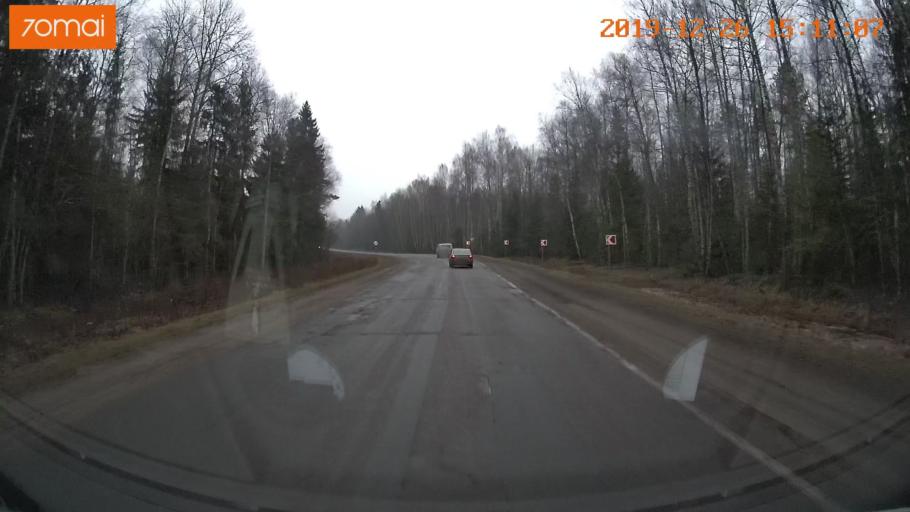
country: RU
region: Jaroslavl
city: Rybinsk
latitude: 58.1360
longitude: 38.8578
